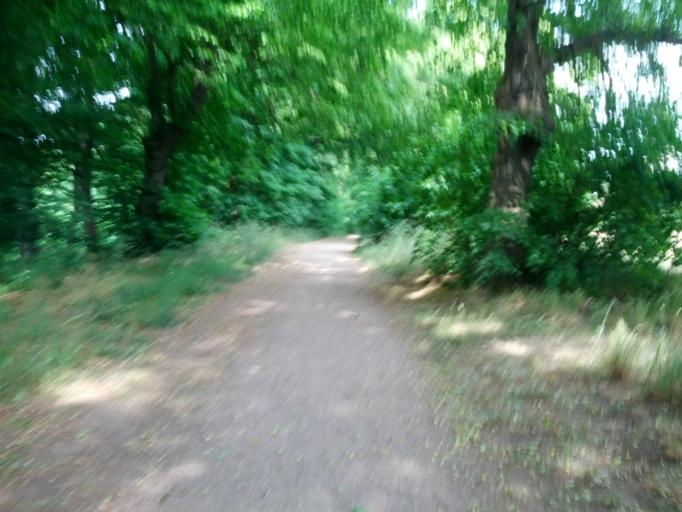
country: DE
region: Thuringia
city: Eisenach
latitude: 50.9658
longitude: 10.3307
